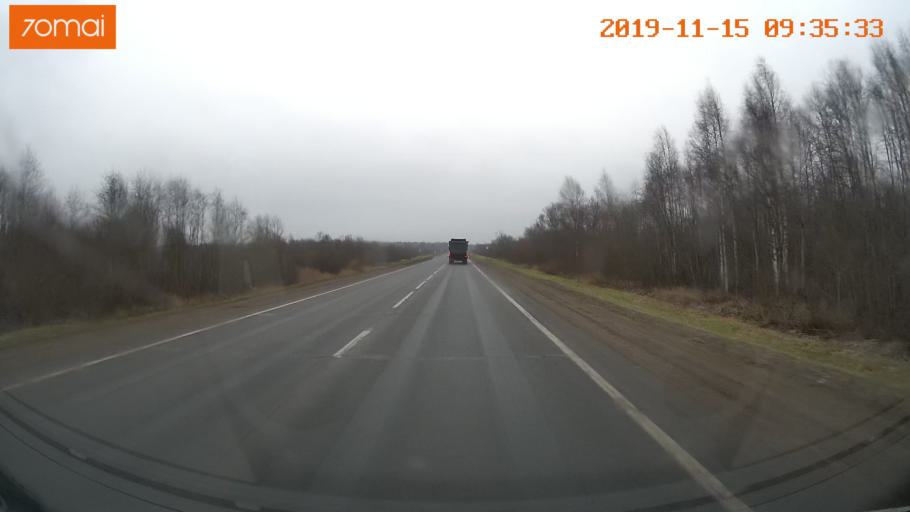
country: RU
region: Vologda
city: Sheksna
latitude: 59.2536
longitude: 38.4020
